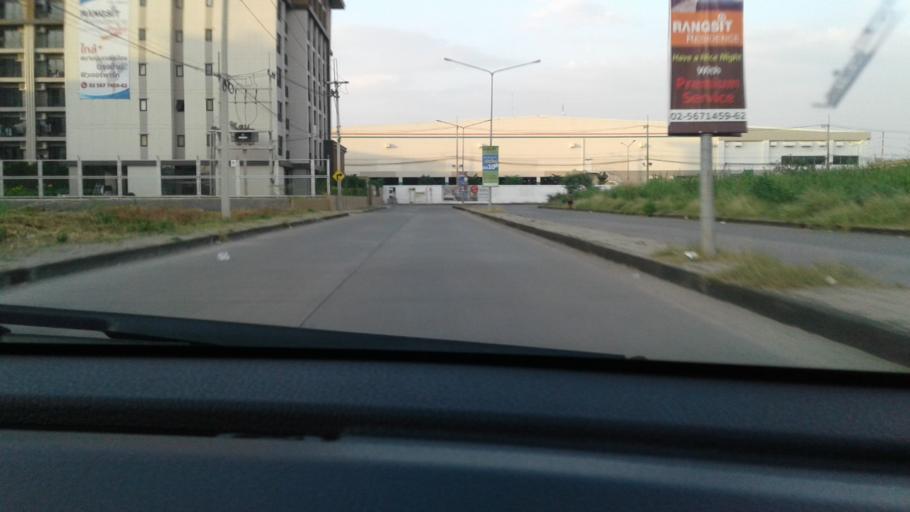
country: TH
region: Phra Nakhon Si Ayutthaya
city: Ban Bang Kadi Pathum Thani
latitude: 13.9918
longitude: 100.6125
